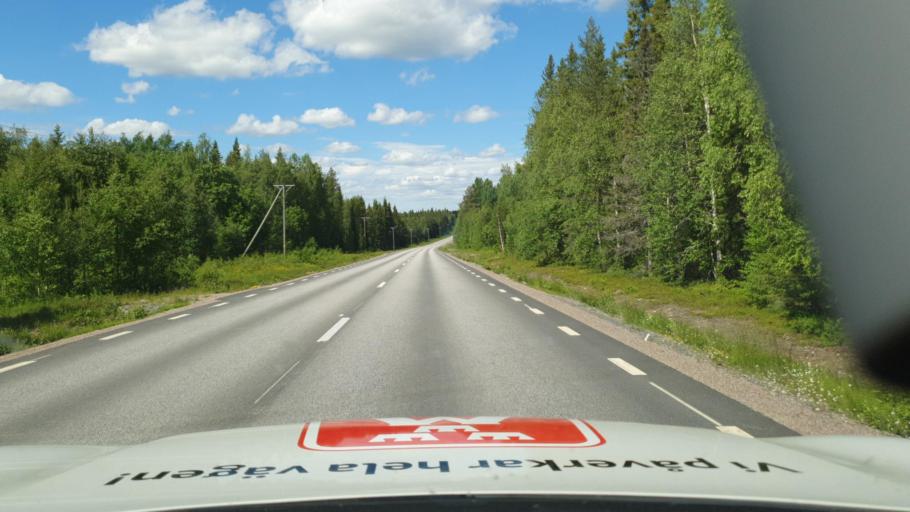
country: SE
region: Vaesterbotten
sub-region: Skelleftea Kommun
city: Boliden
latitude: 64.9197
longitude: 20.3311
